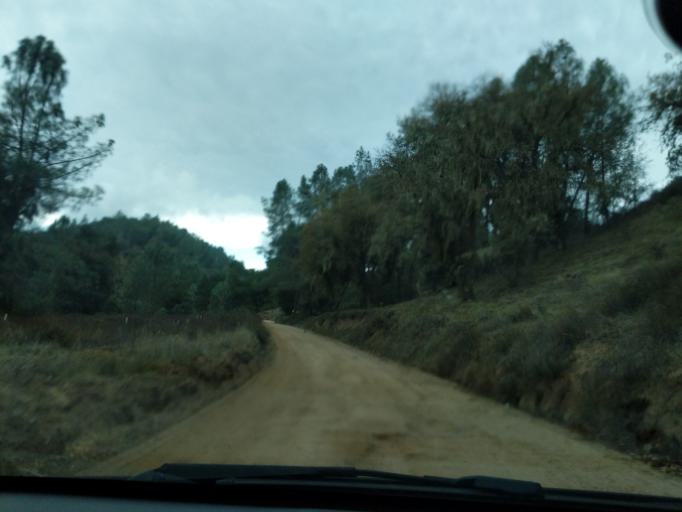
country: US
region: California
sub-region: Monterey County
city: Soledad
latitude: 36.5571
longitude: -121.2400
